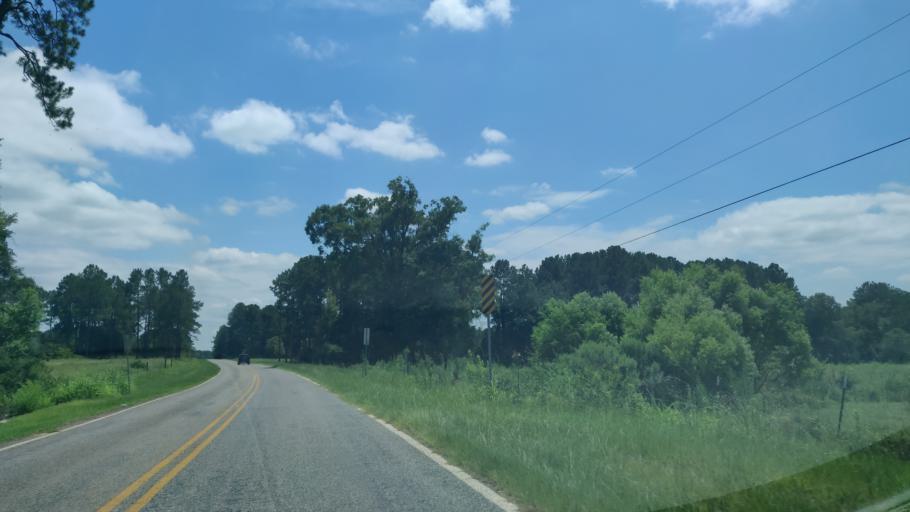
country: US
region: Georgia
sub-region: Tift County
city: Omega
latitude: 31.4424
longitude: -83.6382
